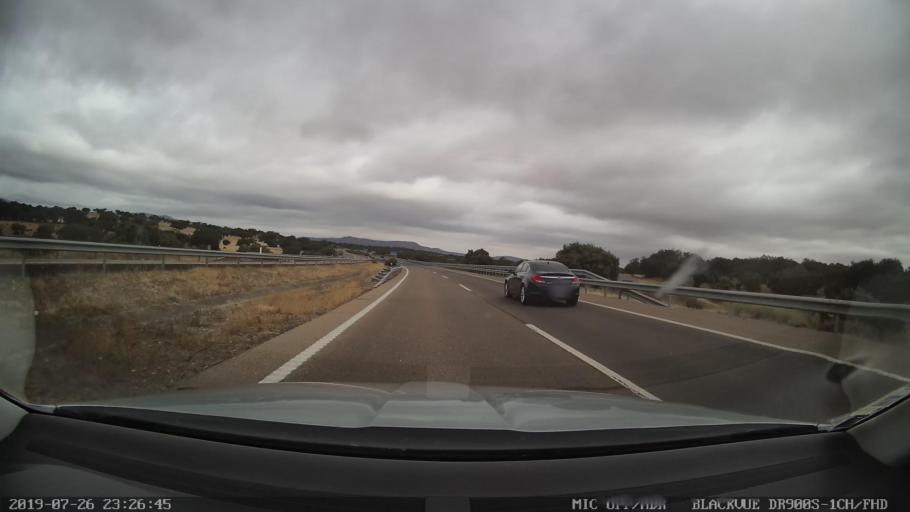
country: ES
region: Extremadura
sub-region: Provincia de Caceres
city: Villamesias
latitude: 39.2139
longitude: -5.8783
